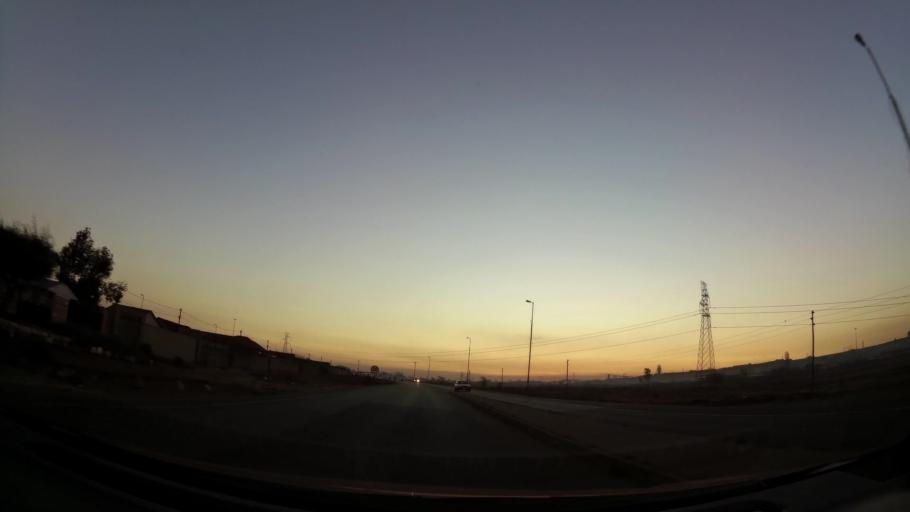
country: ZA
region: Gauteng
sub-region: City of Johannesburg Metropolitan Municipality
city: Soweto
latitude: -26.2297
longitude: 27.8086
